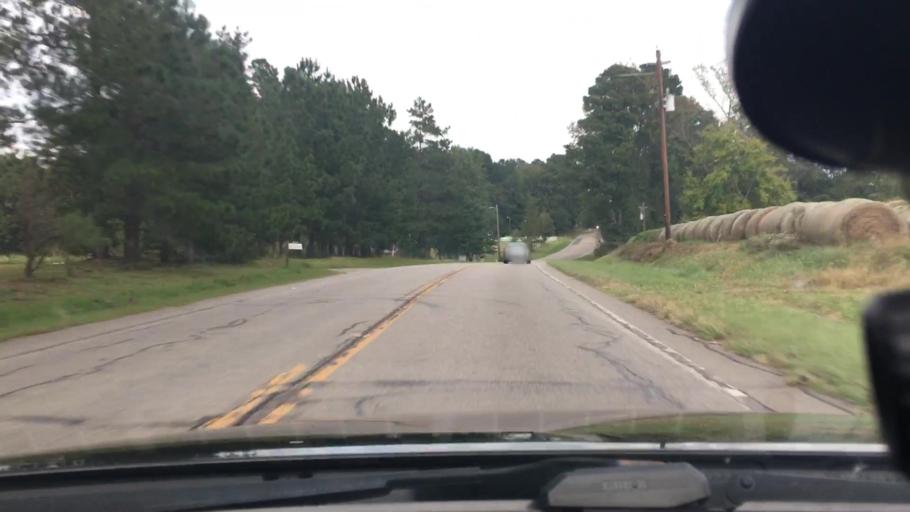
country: US
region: North Carolina
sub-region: Moore County
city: Carthage
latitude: 35.3549
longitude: -79.3455
